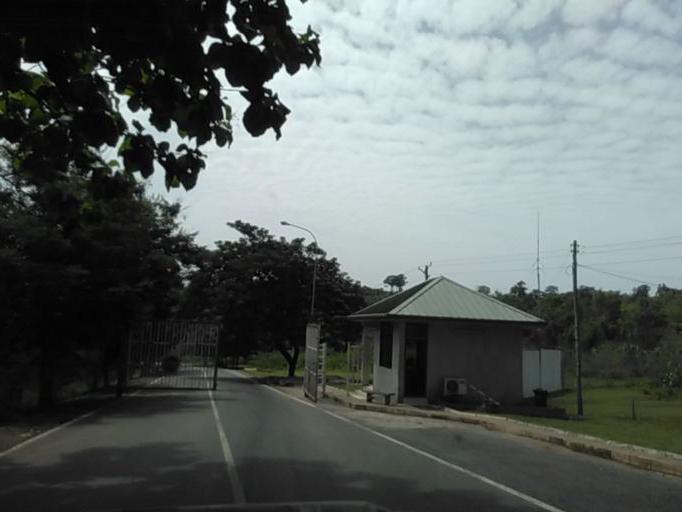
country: GH
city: Akropong
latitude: 6.2638
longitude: 0.0602
